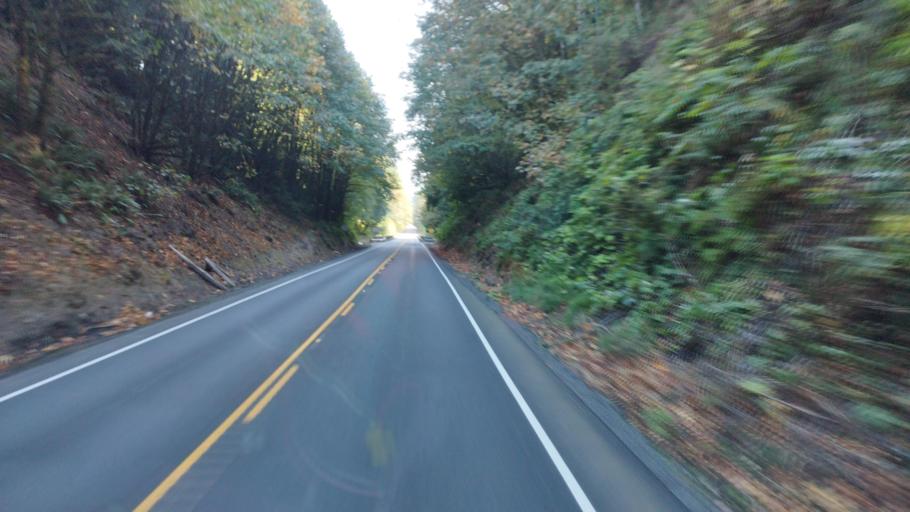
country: US
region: Oregon
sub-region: Columbia County
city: Vernonia
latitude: 45.8593
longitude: -123.5588
